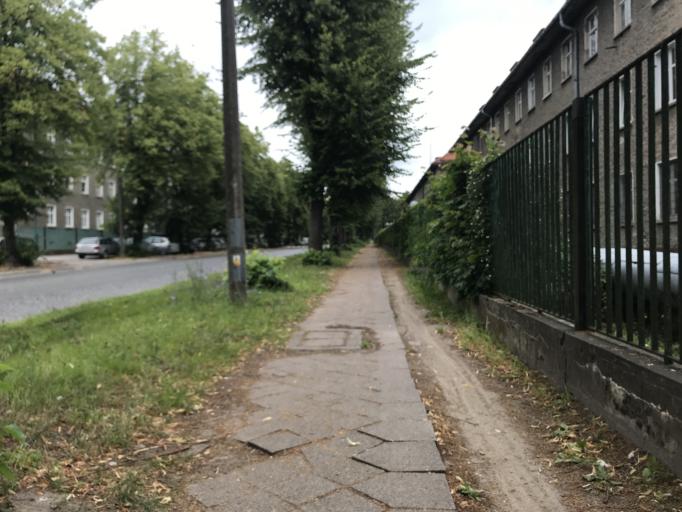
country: PL
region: Warmian-Masurian Voivodeship
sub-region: Powiat elblaski
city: Elblag
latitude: 54.1729
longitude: 19.4155
